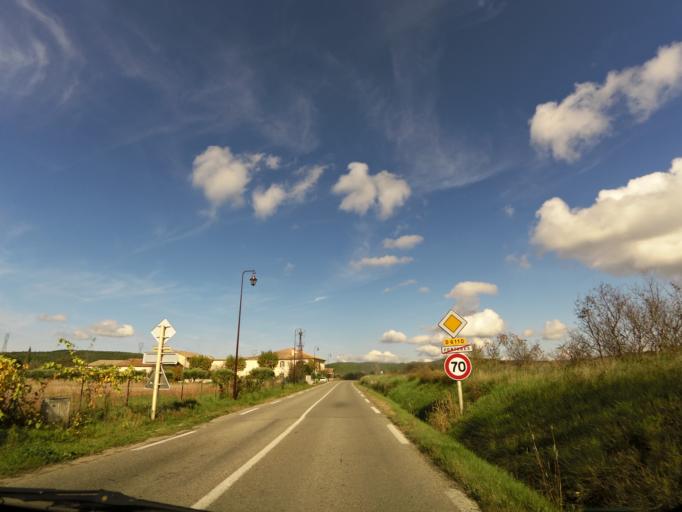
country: FR
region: Languedoc-Roussillon
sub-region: Departement du Gard
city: Villevieille
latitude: 43.8319
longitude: 4.0946
